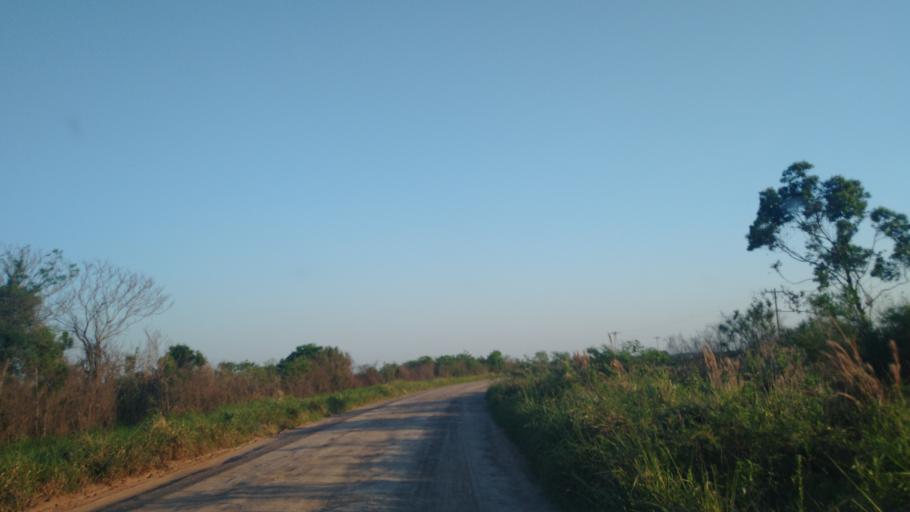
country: PY
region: Neembucu
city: Cerrito
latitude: -27.3944
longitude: -57.6588
